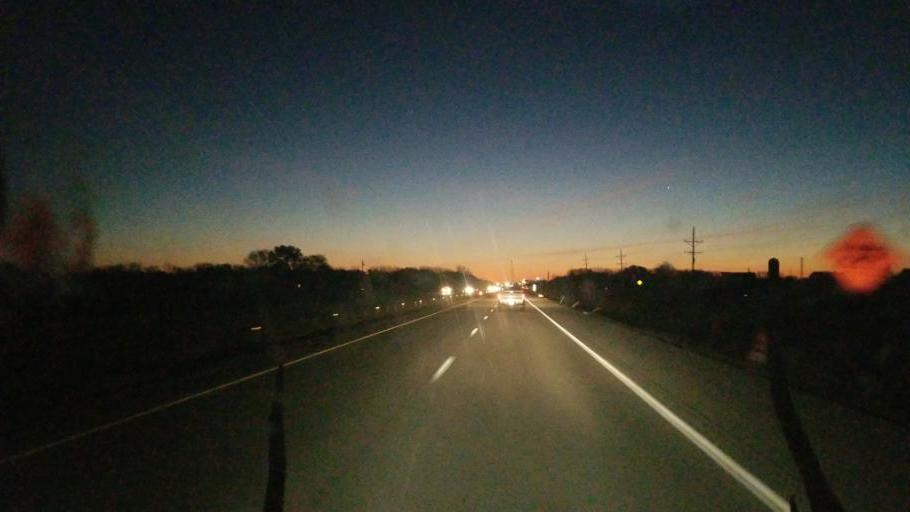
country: US
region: Missouri
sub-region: Saline County
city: Sweet Springs
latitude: 38.9783
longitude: -93.4490
